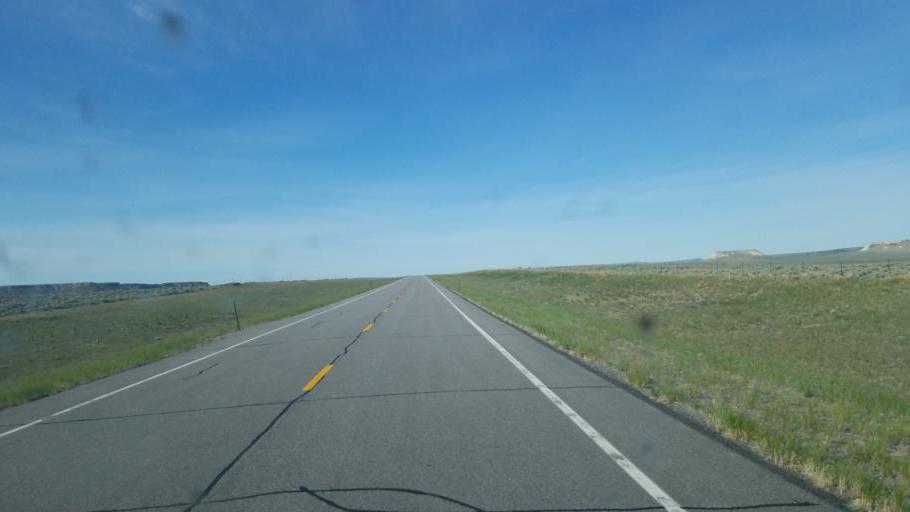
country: US
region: Wyoming
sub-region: Fremont County
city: Riverton
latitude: 42.6673
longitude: -108.1826
